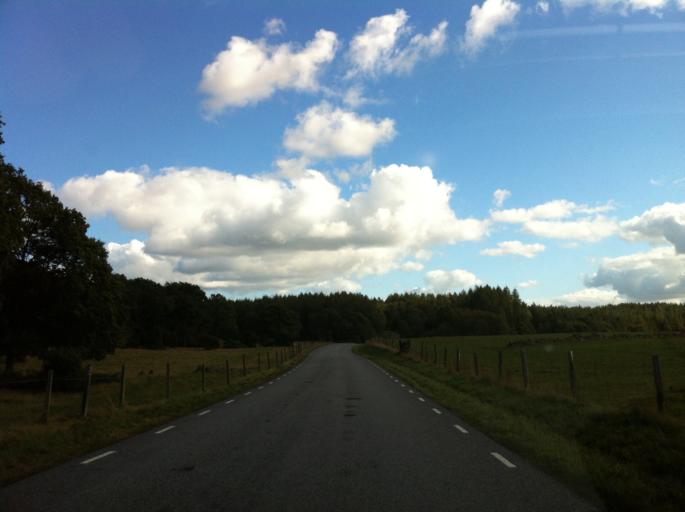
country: SE
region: Skane
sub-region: Kristianstads Kommun
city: Degeberga
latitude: 55.7093
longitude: 13.9833
